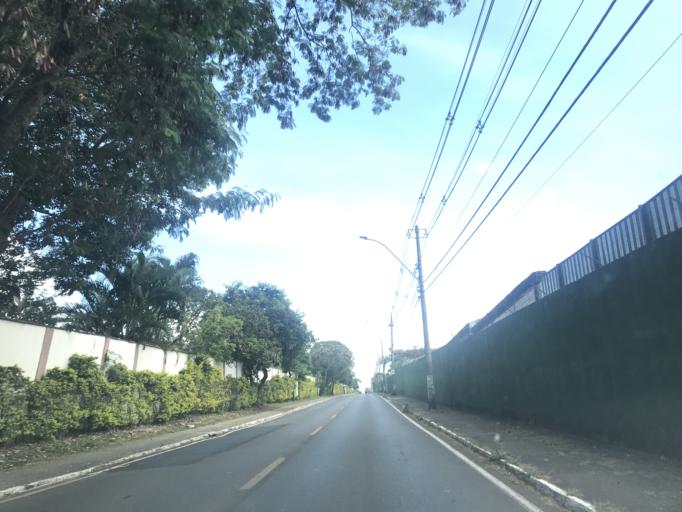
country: BR
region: Federal District
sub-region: Brasilia
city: Brasilia
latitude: -15.8797
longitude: -47.8166
